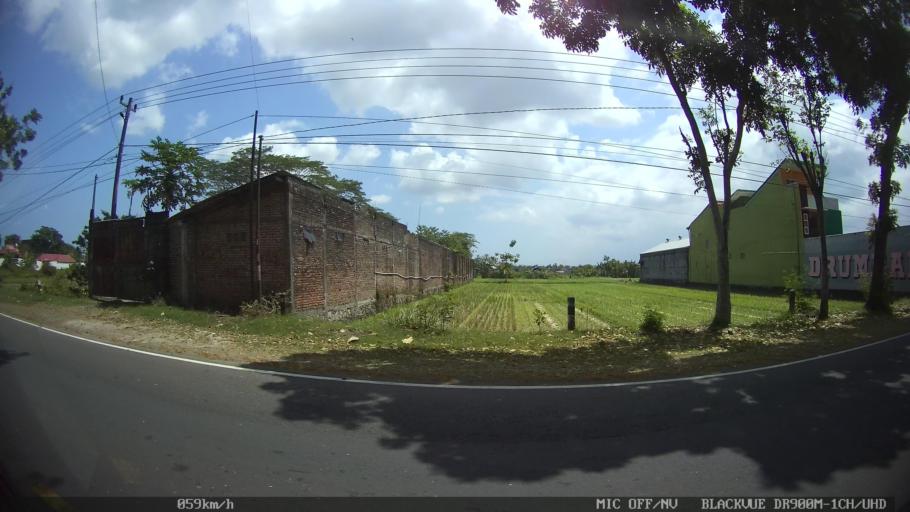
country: ID
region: Daerah Istimewa Yogyakarta
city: Bantul
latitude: -7.8925
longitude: 110.3470
